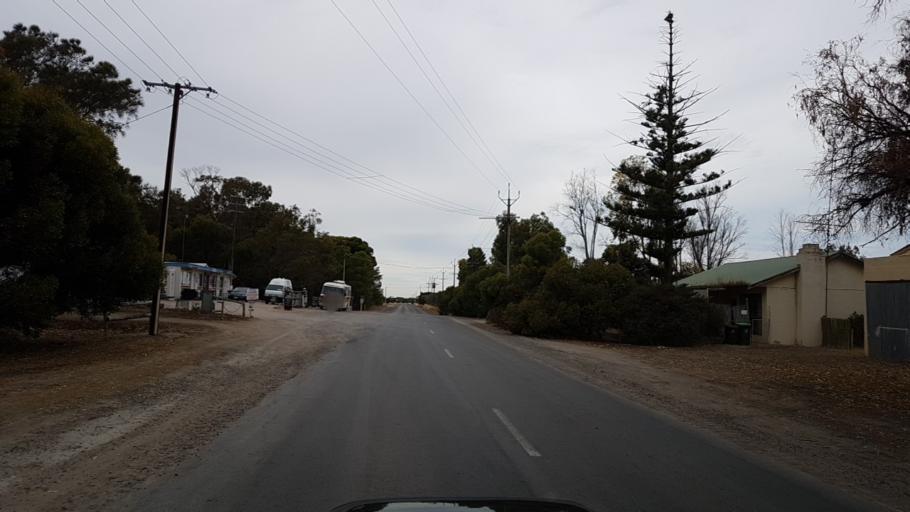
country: AU
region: South Australia
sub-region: Yorke Peninsula
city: Port Victoria
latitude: -34.9157
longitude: 137.0615
